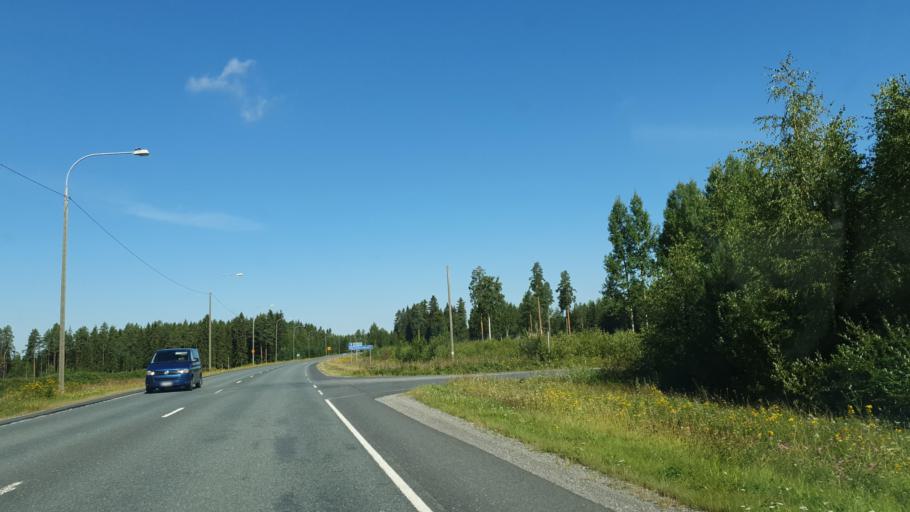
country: FI
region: Northern Savo
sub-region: Kuopio
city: Siilinjaervi
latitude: 63.1905
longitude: 27.5436
